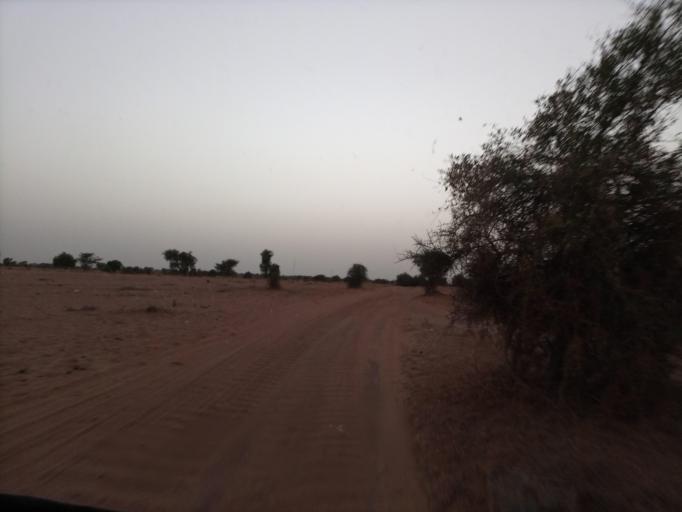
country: SN
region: Louga
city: Dara
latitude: 15.4708
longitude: -15.8465
